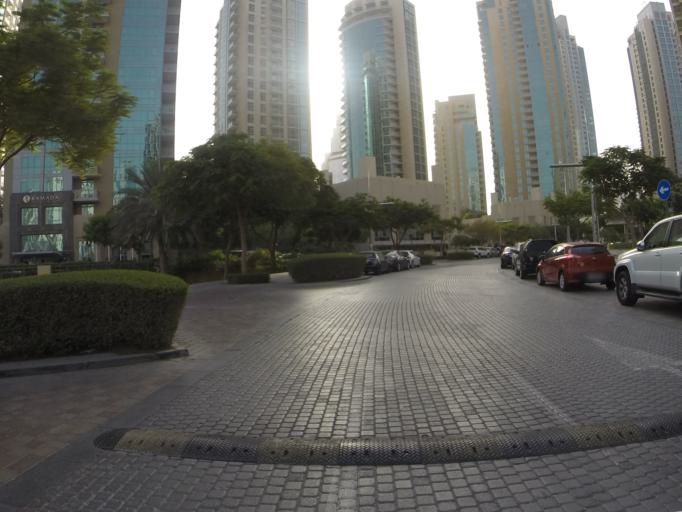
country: AE
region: Dubai
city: Dubai
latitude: 25.1925
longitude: 55.2722
